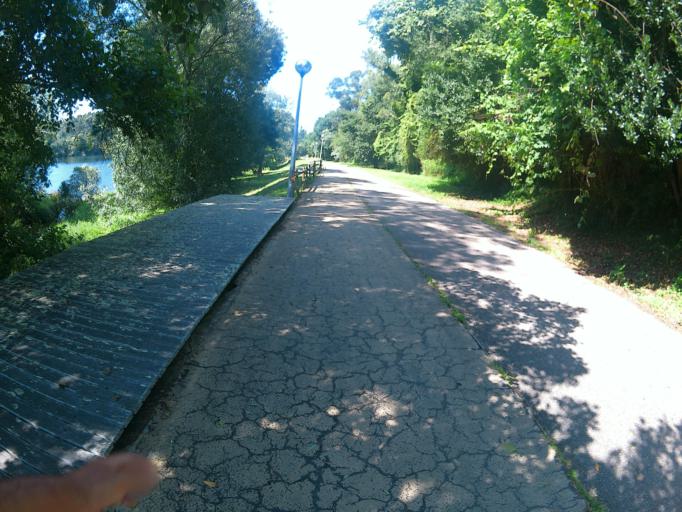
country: PT
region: Viana do Castelo
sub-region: Valenca
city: Valenca
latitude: 42.0159
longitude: -8.6562
